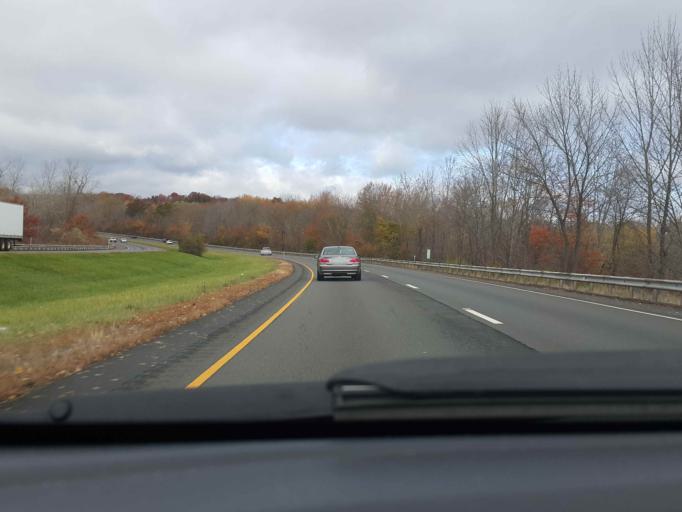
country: US
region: Connecticut
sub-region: Middlesex County
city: Cromwell
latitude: 41.5902
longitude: -72.6515
